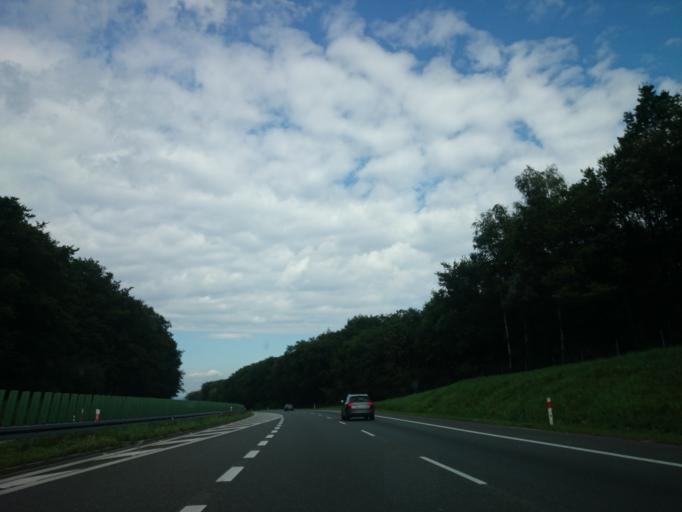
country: PL
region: Opole Voivodeship
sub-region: Powiat krapkowicki
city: Zdzieszowice
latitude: 50.4669
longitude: 18.1512
